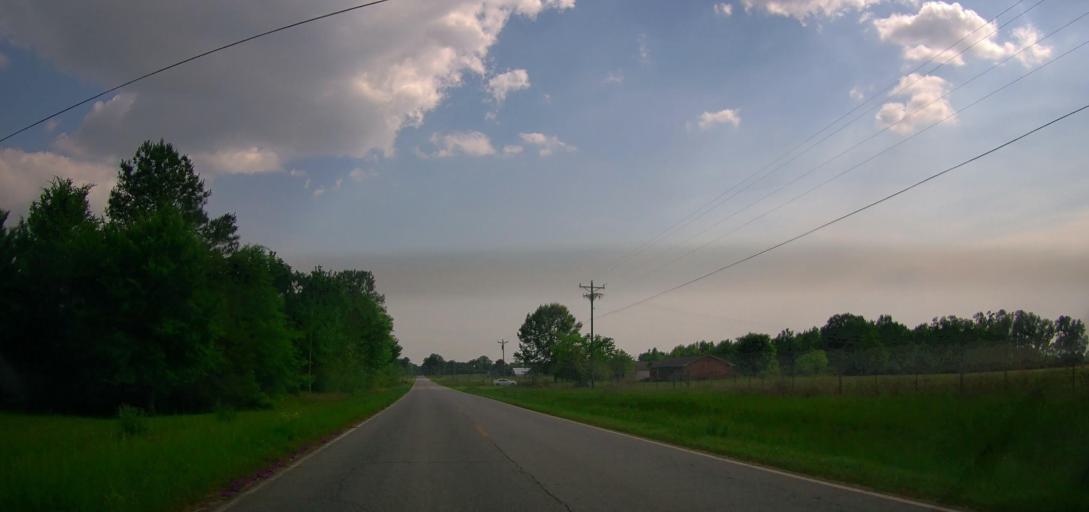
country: US
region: Georgia
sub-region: Laurens County
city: East Dublin
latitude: 32.6060
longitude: -82.8676
